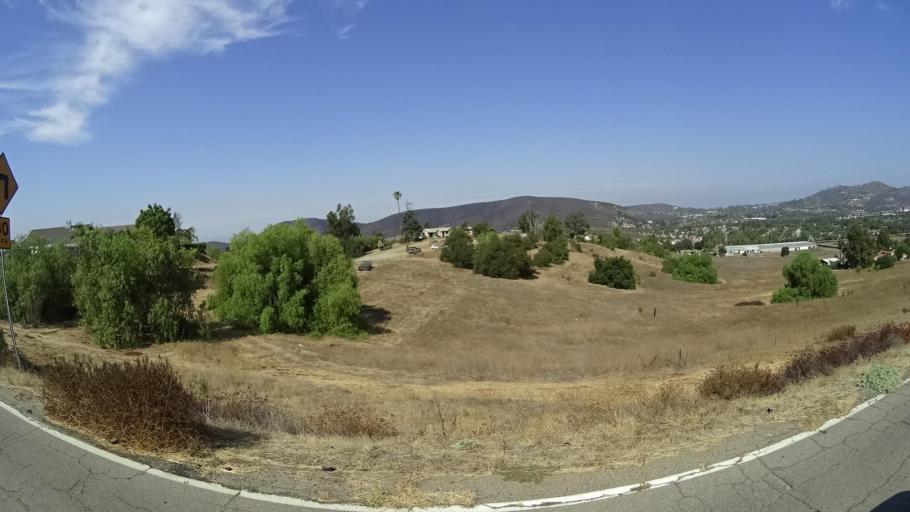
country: US
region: California
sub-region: San Diego County
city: San Marcos
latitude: 33.1651
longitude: -117.1459
